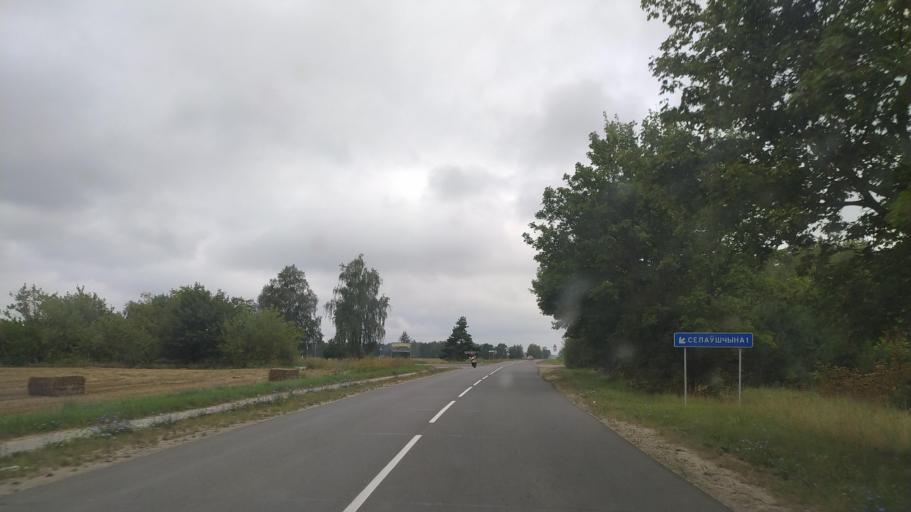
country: BY
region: Brest
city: Byaroza
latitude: 52.5568
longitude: 24.9163
